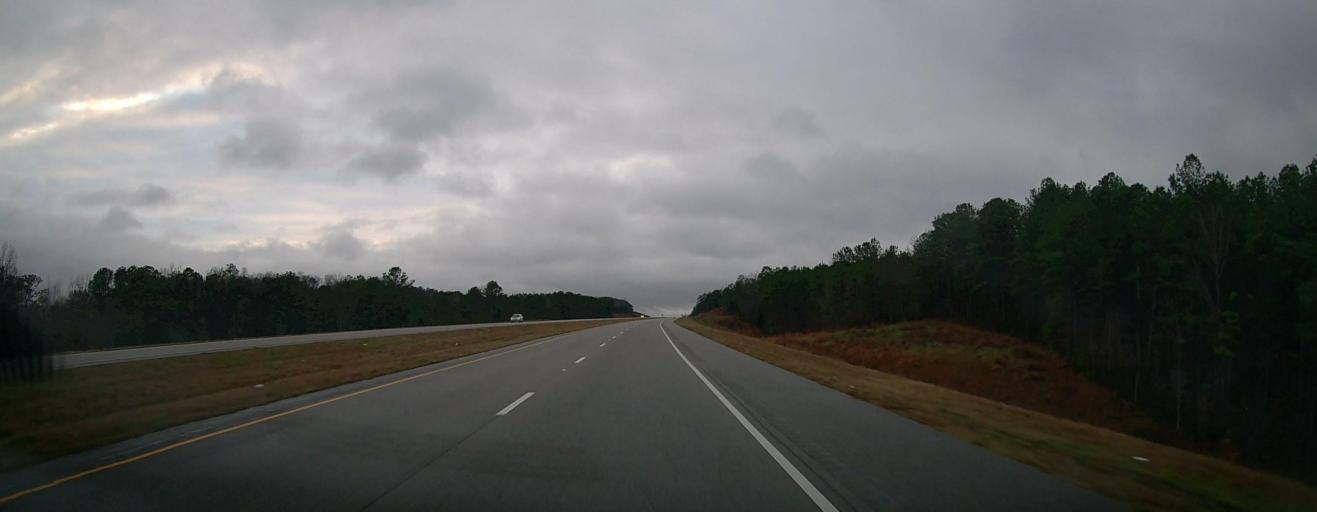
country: US
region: Alabama
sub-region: Bibb County
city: Centreville
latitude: 32.9479
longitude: -87.0985
